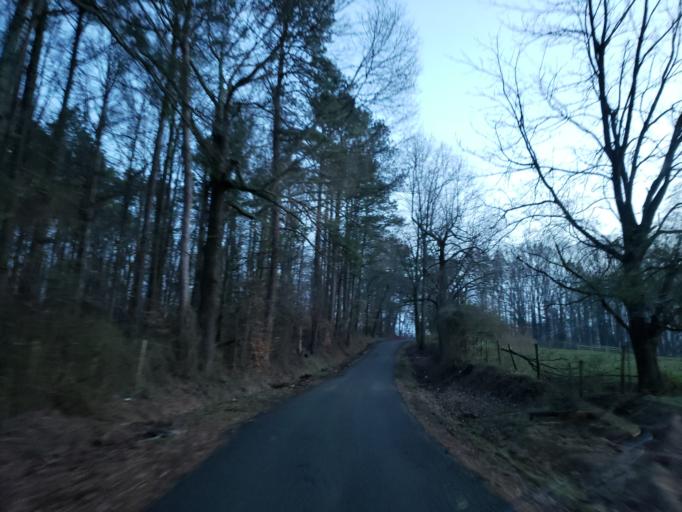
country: US
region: Georgia
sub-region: Cherokee County
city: Ball Ground
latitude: 34.2901
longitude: -84.2810
